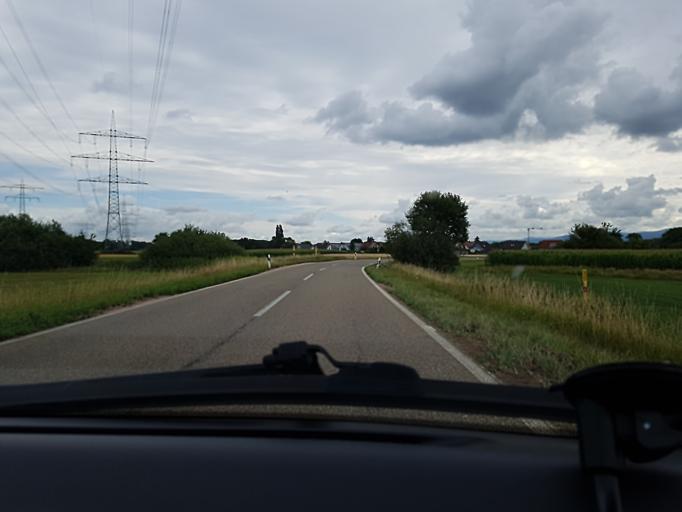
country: DE
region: Baden-Wuerttemberg
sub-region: Freiburg Region
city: Rheinau
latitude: 48.6074
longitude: 7.8971
